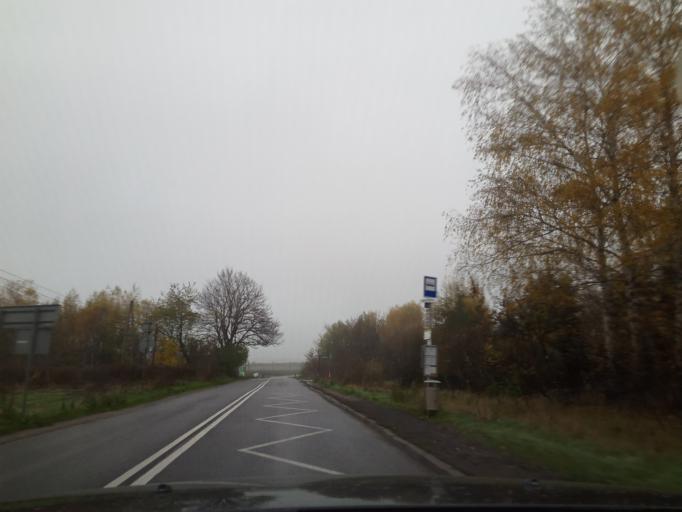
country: PL
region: Lesser Poland Voivodeship
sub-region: Powiat wielicki
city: Kokotow
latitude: 50.1044
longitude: 20.0728
